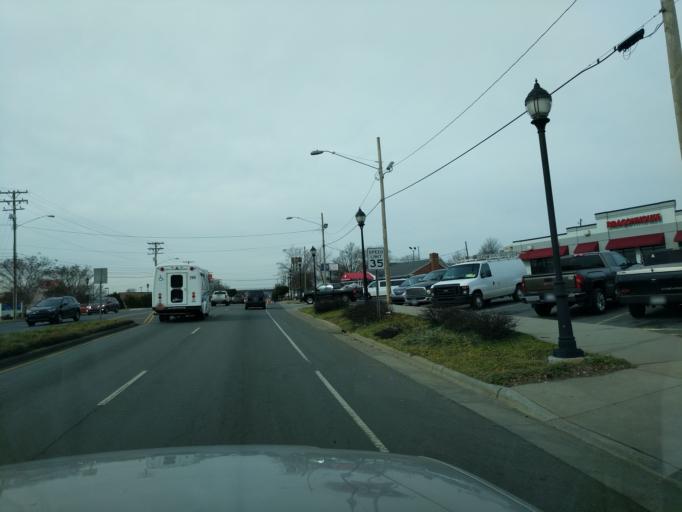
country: US
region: North Carolina
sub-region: Mecklenburg County
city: Charlotte
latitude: 35.1765
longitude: -80.8755
